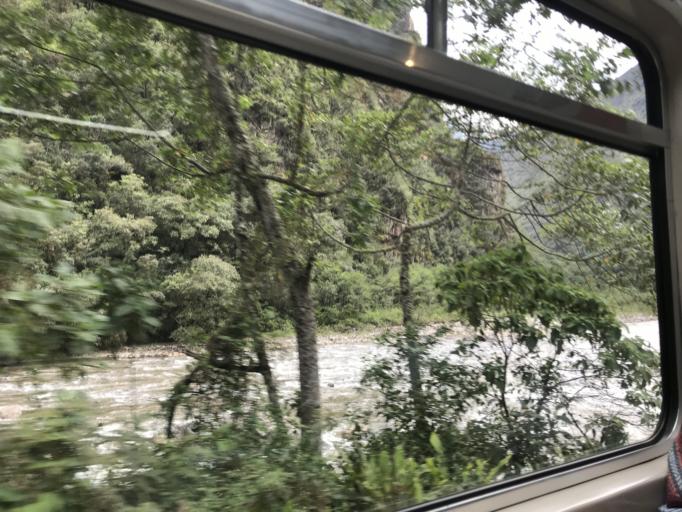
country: PE
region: Cusco
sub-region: Provincia de La Convencion
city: Santa Teresa
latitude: -13.1710
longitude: -72.5022
